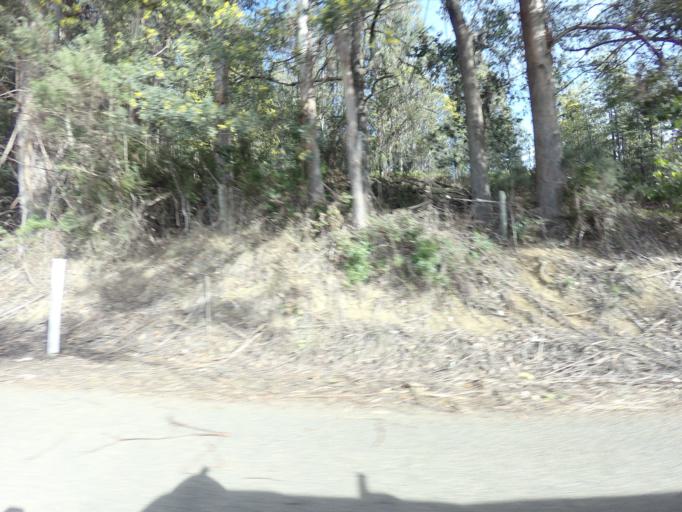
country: AU
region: Tasmania
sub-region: Kingborough
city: Margate
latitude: -43.0150
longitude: 147.1610
